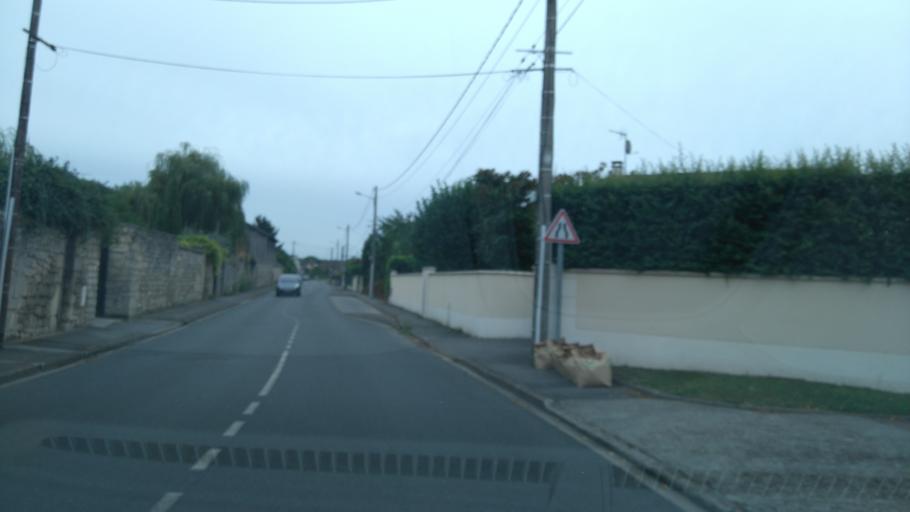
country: FR
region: Picardie
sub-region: Departement de l'Oise
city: Villers-sous-Saint-Leu
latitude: 49.2151
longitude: 2.4156
